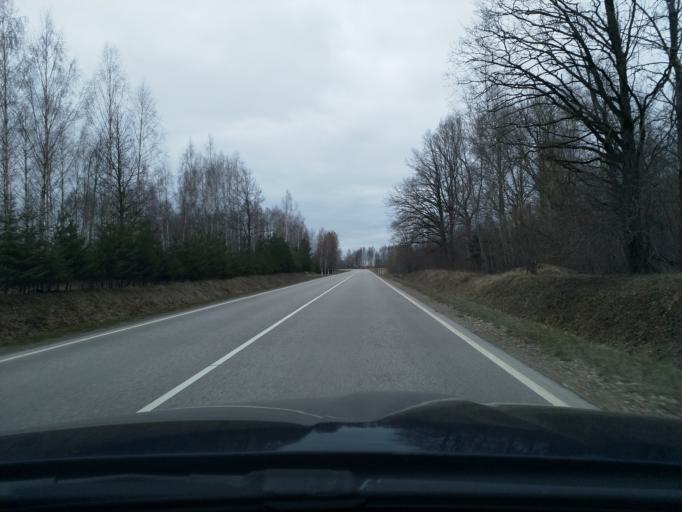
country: LV
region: Talsu Rajons
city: Sabile
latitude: 56.9473
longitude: 22.4780
